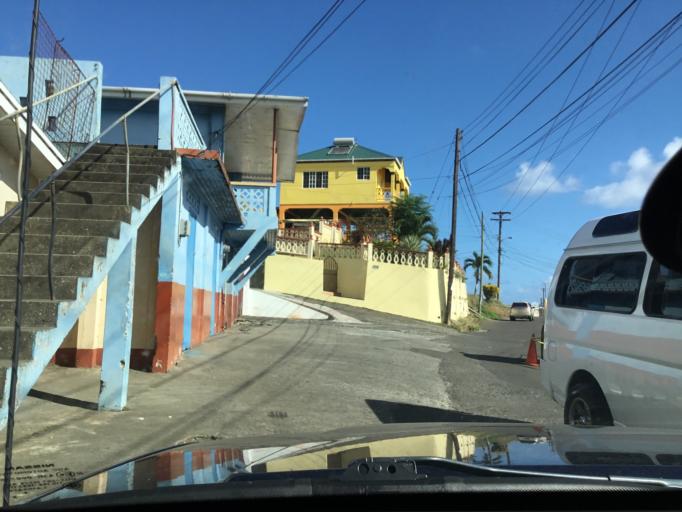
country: VC
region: Charlotte
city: Biabou
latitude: 13.1598
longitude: -61.1589
